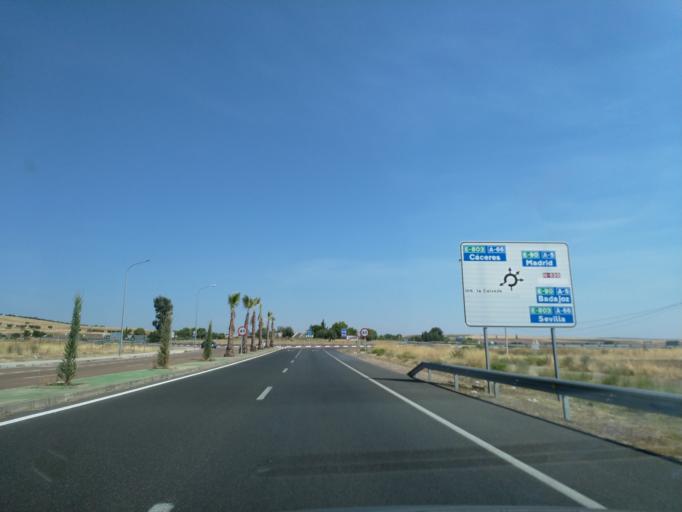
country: ES
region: Extremadura
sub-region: Provincia de Badajoz
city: Merida
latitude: 38.9388
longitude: -6.3438
